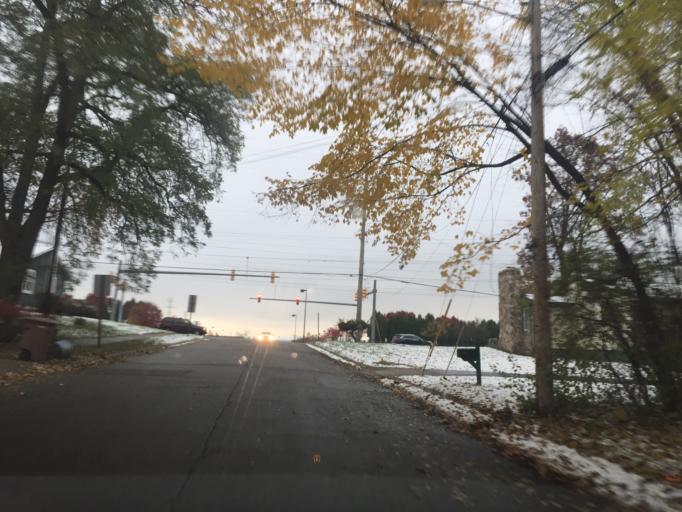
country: US
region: Michigan
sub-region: Oakland County
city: Pontiac
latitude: 42.6227
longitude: -83.2695
